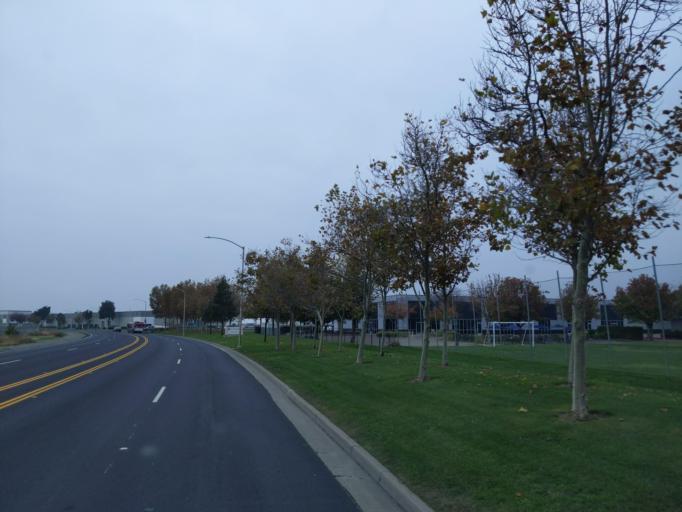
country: US
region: California
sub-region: San Joaquin County
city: Kennedy
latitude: 37.9063
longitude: -121.2318
